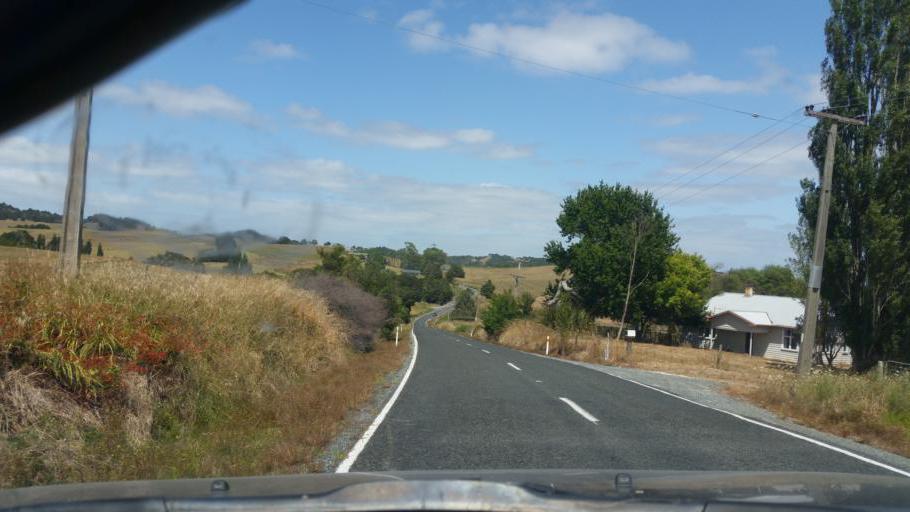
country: NZ
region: Northland
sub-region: Whangarei
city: Ruakaka
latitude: -36.0128
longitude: 174.2910
